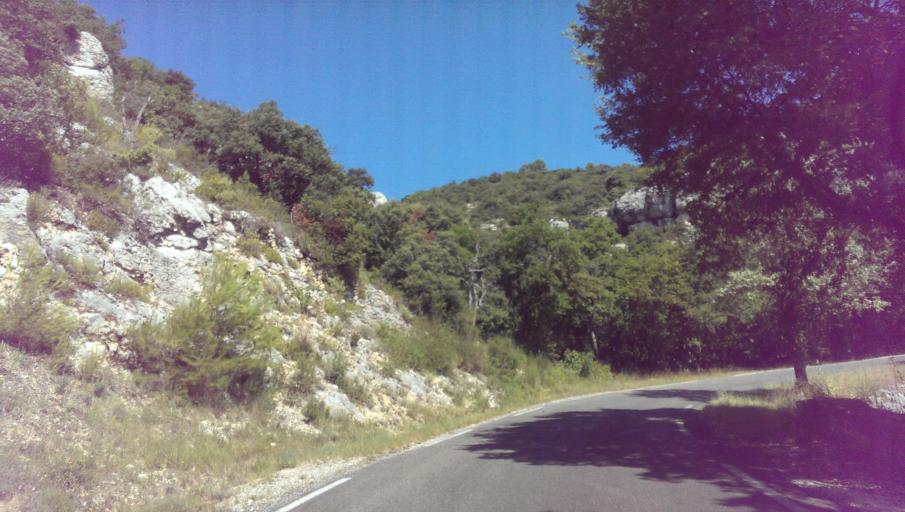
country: FR
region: Provence-Alpes-Cote d'Azur
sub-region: Departement du Vaucluse
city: Gordes
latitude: 43.9365
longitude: 5.1877
